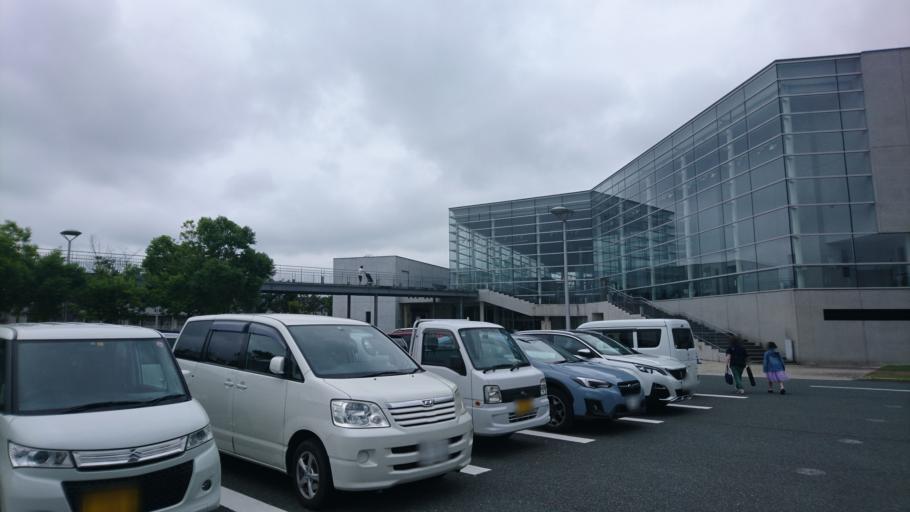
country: JP
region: Iwate
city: Kitakami
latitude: 39.2976
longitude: 141.1107
